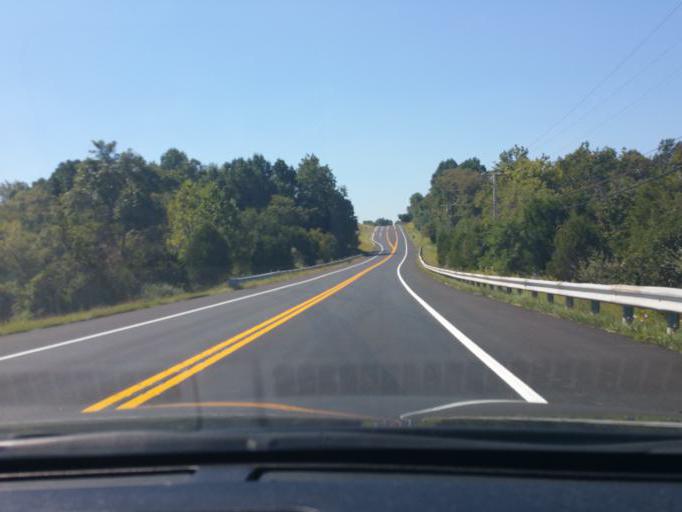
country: US
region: Maryland
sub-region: Harford County
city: Aberdeen
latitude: 39.5667
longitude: -76.2315
